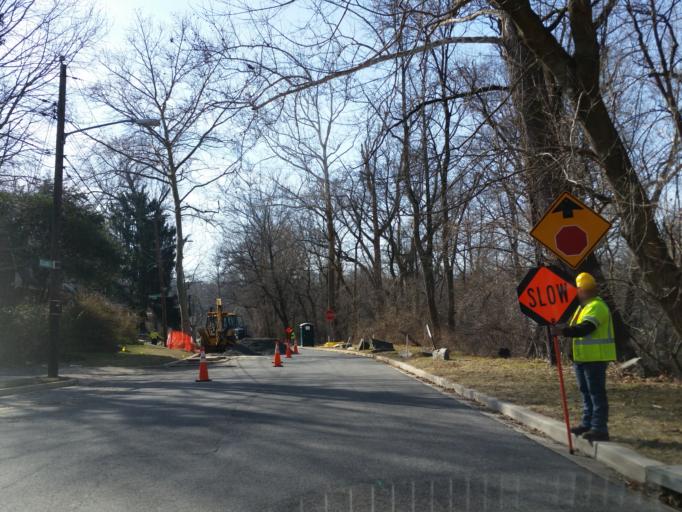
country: US
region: Maryland
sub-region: Montgomery County
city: Silver Spring
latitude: 38.9894
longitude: -77.0394
